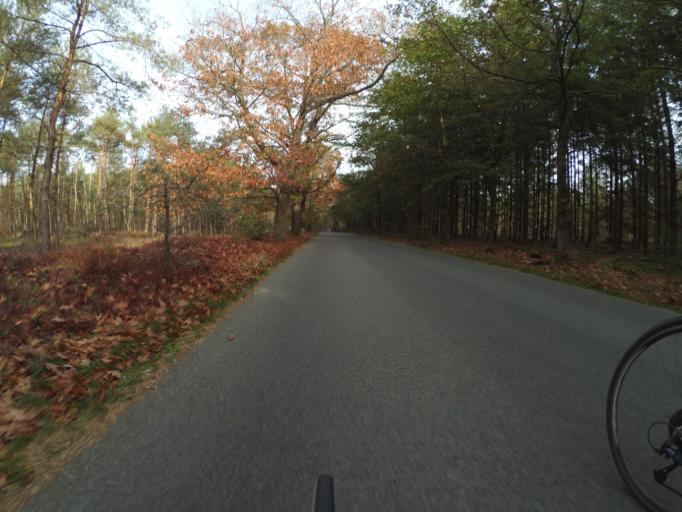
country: NL
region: Overijssel
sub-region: Gemeente Hof van Twente
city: Markelo
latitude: 52.3340
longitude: 6.4229
